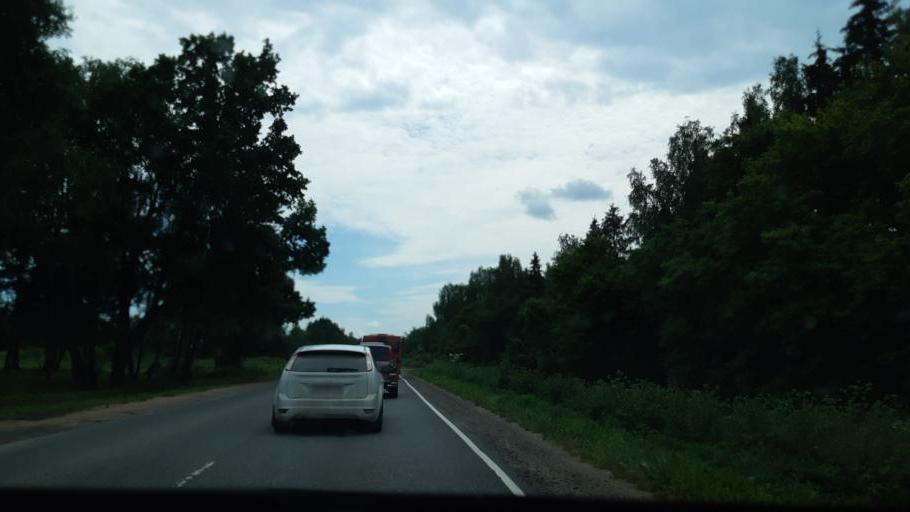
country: RU
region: Moskovskaya
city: Vereya
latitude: 55.3951
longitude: 36.3208
